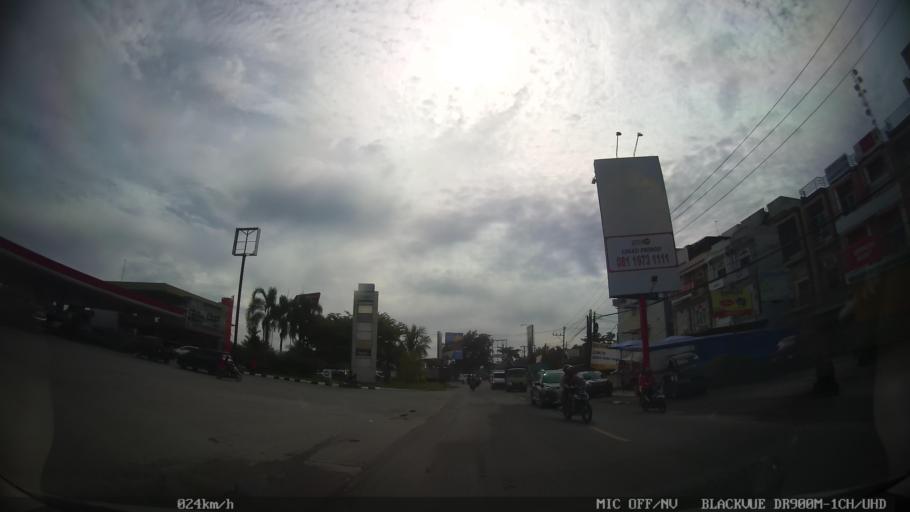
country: ID
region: North Sumatra
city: Medan
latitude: 3.6285
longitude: 98.7070
